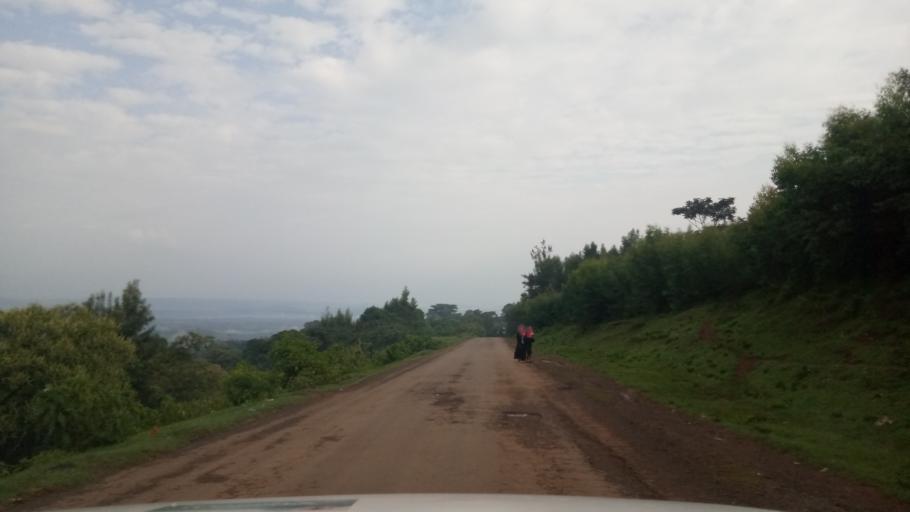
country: ET
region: Oromiya
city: Agaro
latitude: 7.7939
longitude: 36.7238
